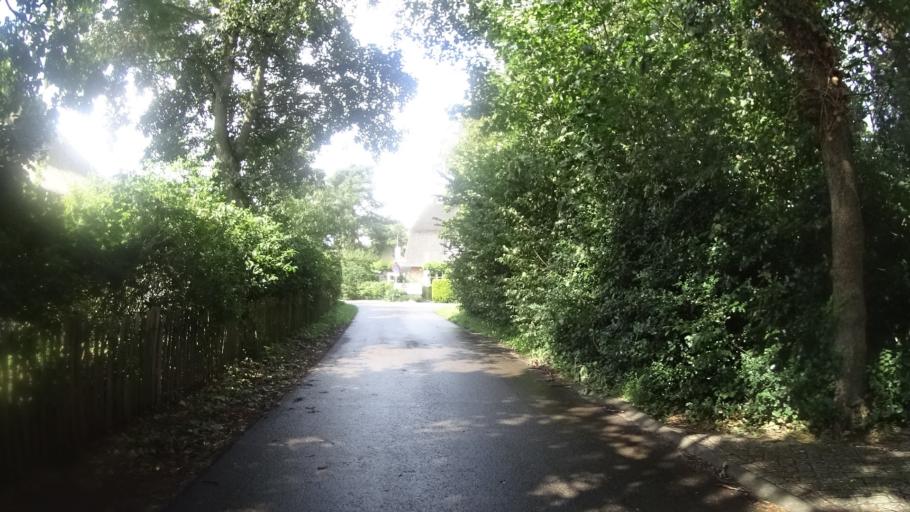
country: NL
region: North Holland
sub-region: Gemeente Alkmaar
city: Alkmaar
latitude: 52.6998
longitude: 4.6981
